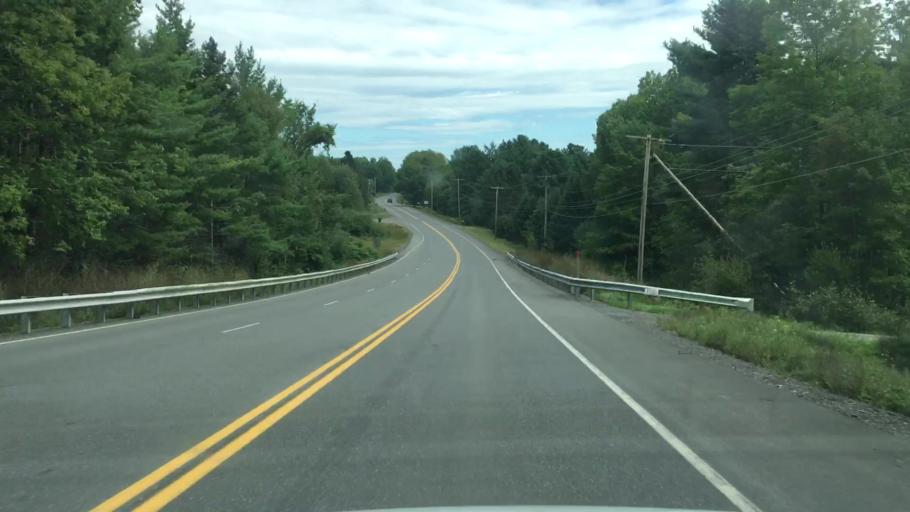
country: US
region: Maine
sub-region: Piscataquis County
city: Milo
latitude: 45.2375
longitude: -69.0518
